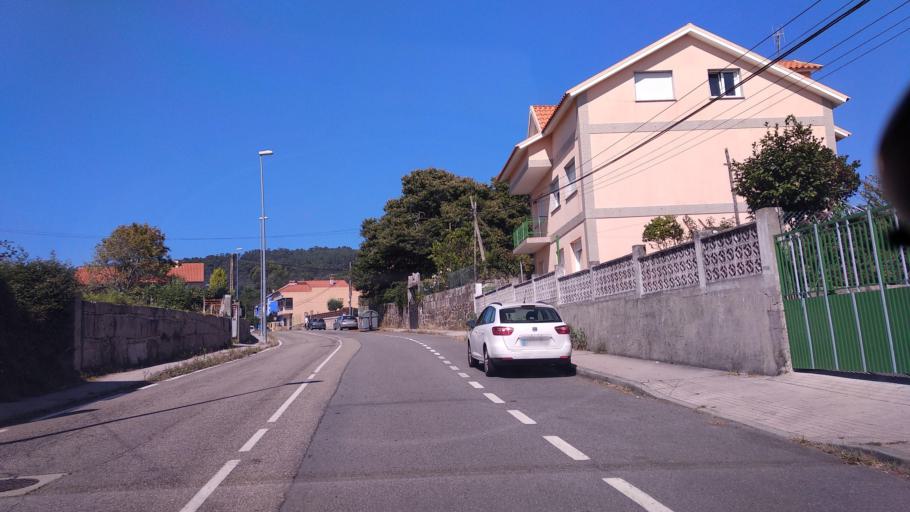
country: ES
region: Galicia
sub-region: Provincia de Pontevedra
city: Cangas
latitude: 42.2706
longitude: -8.7678
